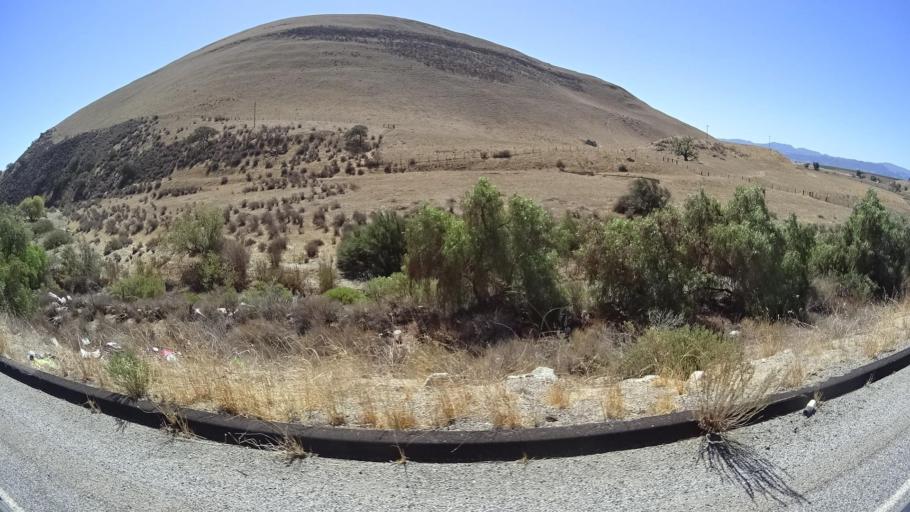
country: US
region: California
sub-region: Monterey County
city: King City
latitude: 36.2683
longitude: -121.0739
